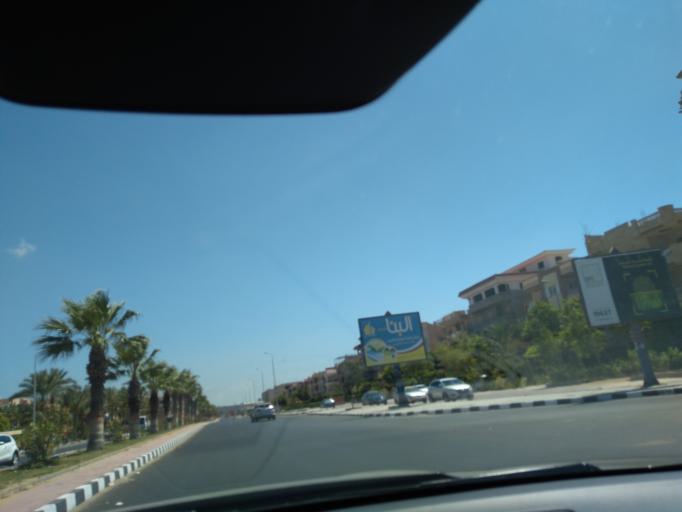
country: EG
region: Dumyat
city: Faraskur
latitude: 31.4295
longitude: 31.6739
